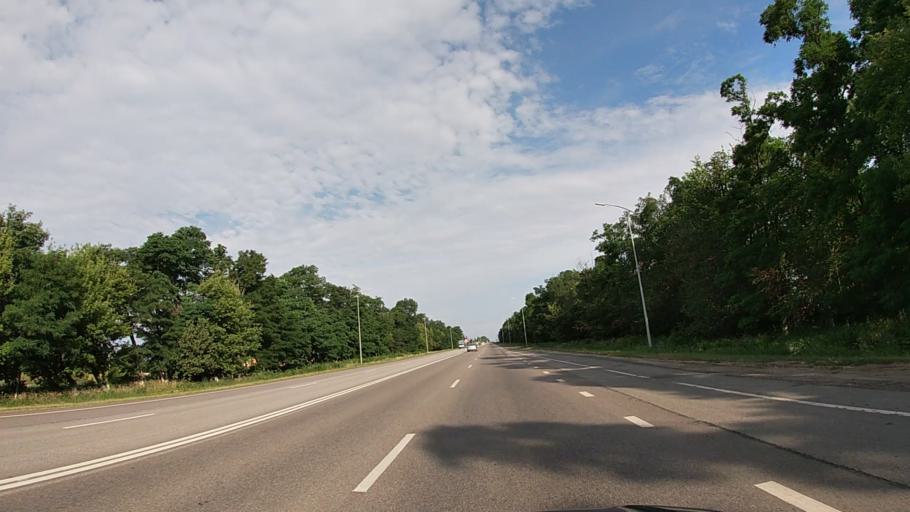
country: RU
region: Belgorod
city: Severnyy
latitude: 50.6394
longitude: 36.4408
